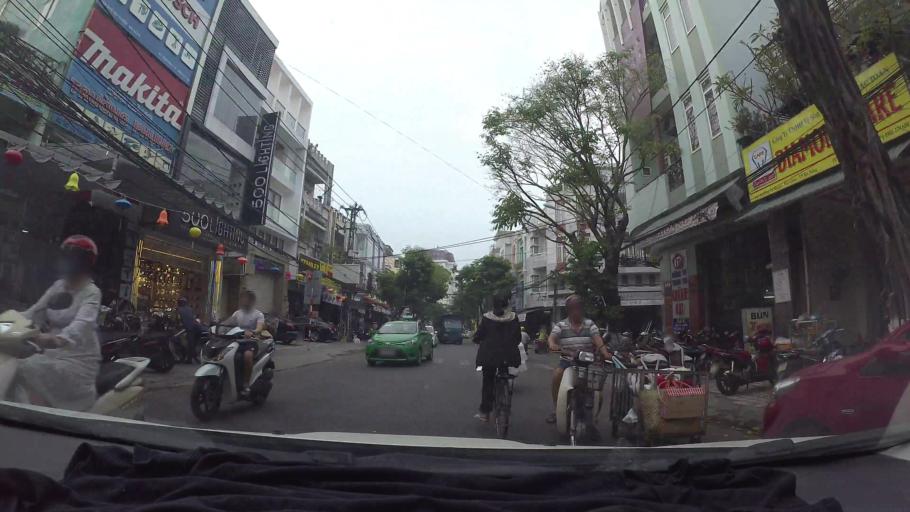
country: VN
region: Da Nang
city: Da Nang
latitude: 16.0645
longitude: 108.2151
